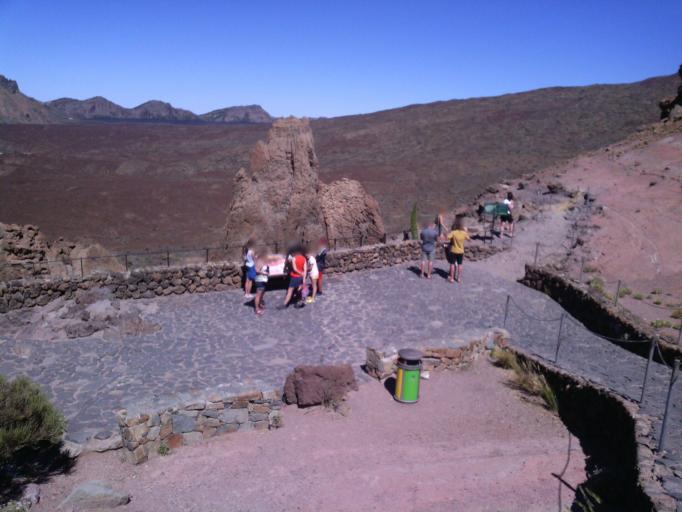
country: ES
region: Canary Islands
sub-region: Provincia de Santa Cruz de Tenerife
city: Vilaflor
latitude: 28.2230
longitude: -16.6310
